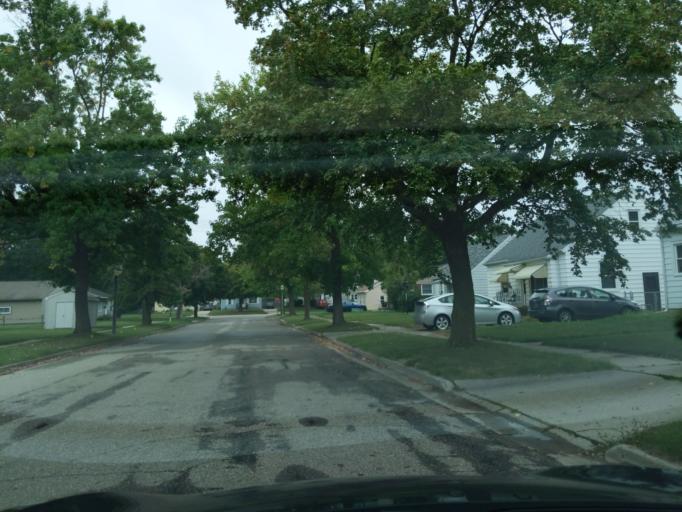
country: US
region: Michigan
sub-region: Ingham County
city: Lansing
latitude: 42.6934
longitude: -84.5368
